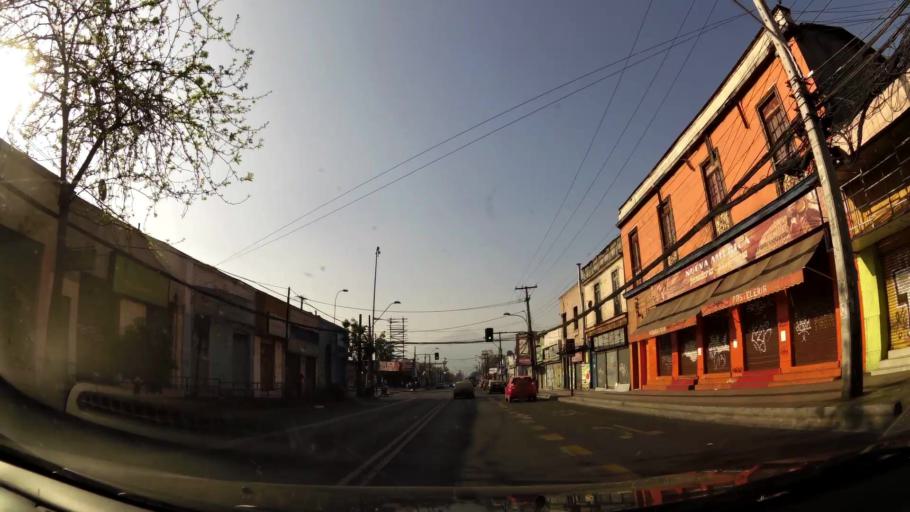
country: CL
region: Santiago Metropolitan
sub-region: Provincia de Santiago
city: Santiago
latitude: -33.4063
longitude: -70.6431
